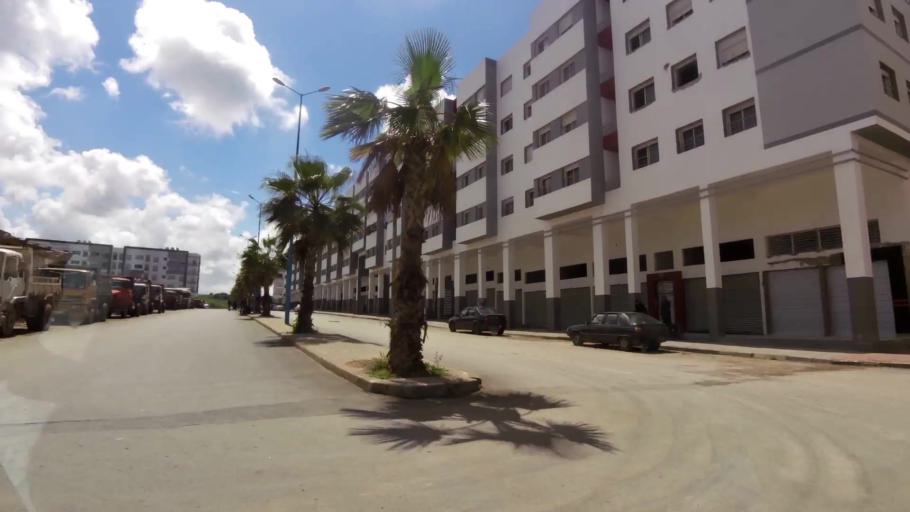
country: MA
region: Grand Casablanca
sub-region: Nouaceur
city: Dar Bouazza
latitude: 33.5304
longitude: -7.7359
